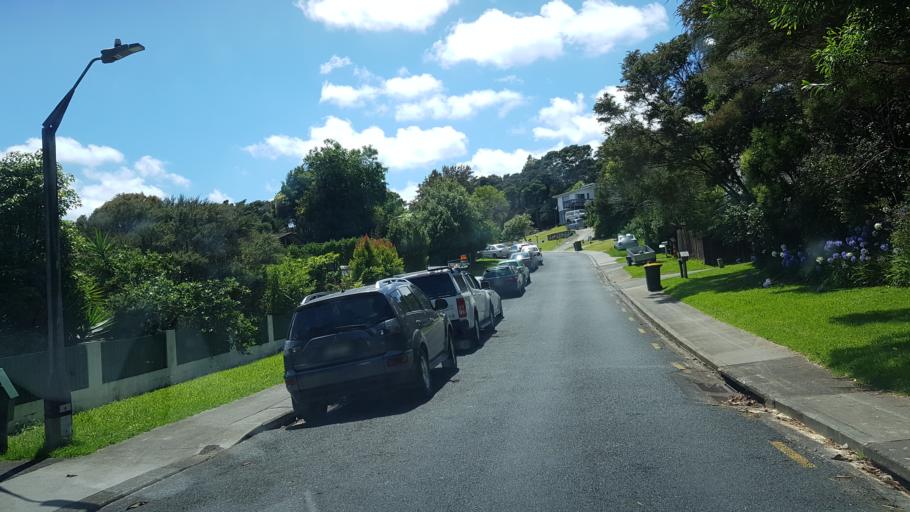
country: NZ
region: Auckland
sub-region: Auckland
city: North Shore
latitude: -36.7885
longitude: 174.7141
